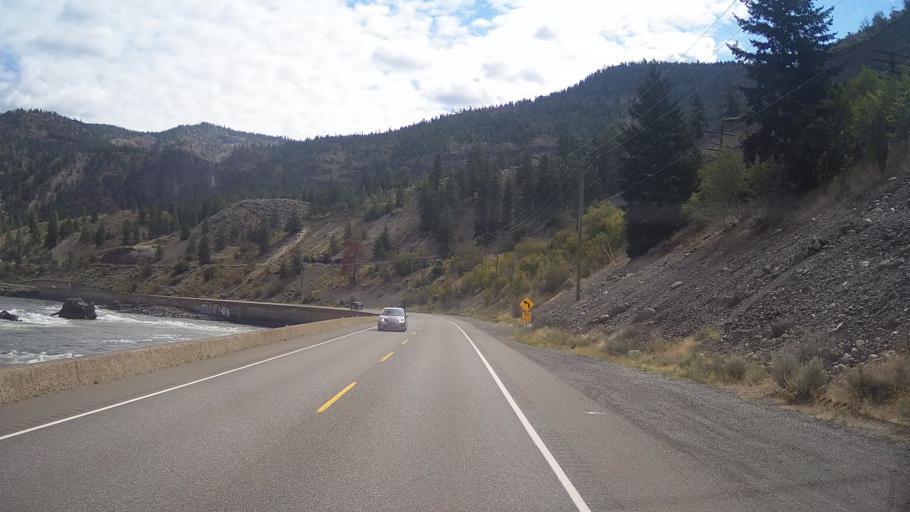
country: CA
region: British Columbia
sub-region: Thompson-Nicola Regional District
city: Ashcroft
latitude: 50.2631
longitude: -121.4094
